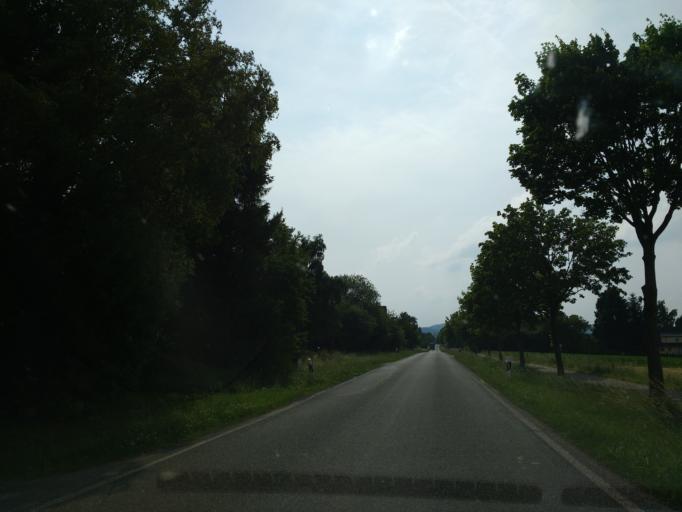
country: DE
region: North Rhine-Westphalia
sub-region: Regierungsbezirk Detmold
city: Horn-Bad Meinberg
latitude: 51.8769
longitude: 8.9723
